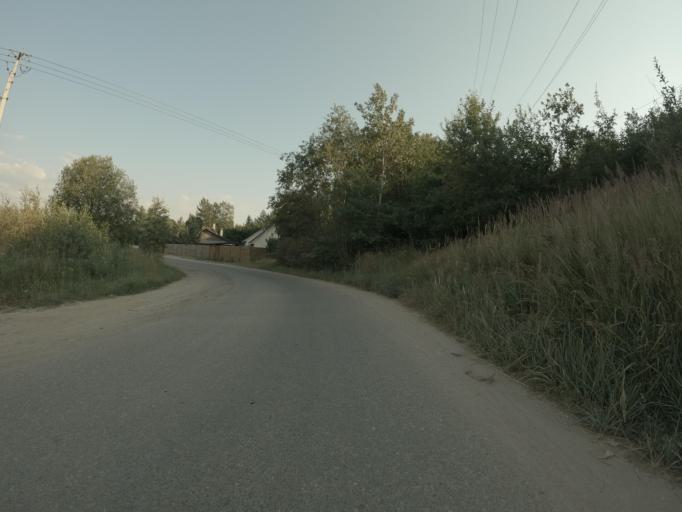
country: RU
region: Leningrad
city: Koltushi
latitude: 59.8946
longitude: 30.6880
